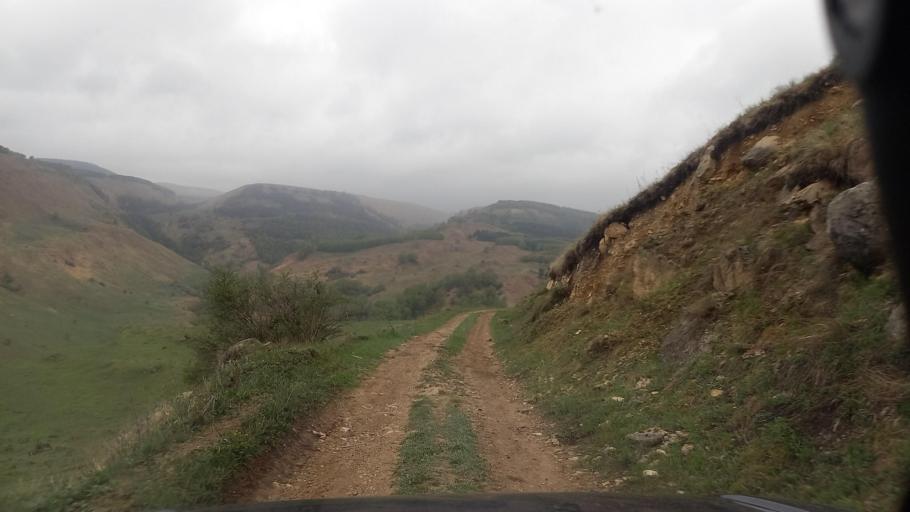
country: RU
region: Stavropol'skiy
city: Nezhinskiy
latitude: 43.8520
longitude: 42.6387
